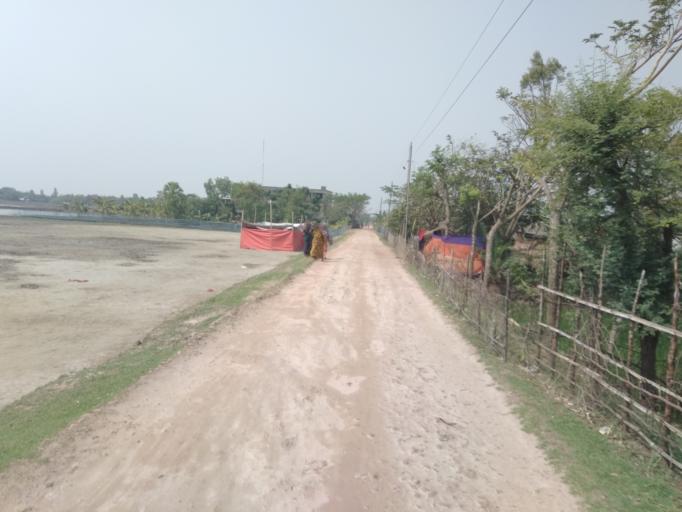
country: IN
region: West Bengal
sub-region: North 24 Parganas
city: Taki
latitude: 22.3032
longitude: 89.2675
